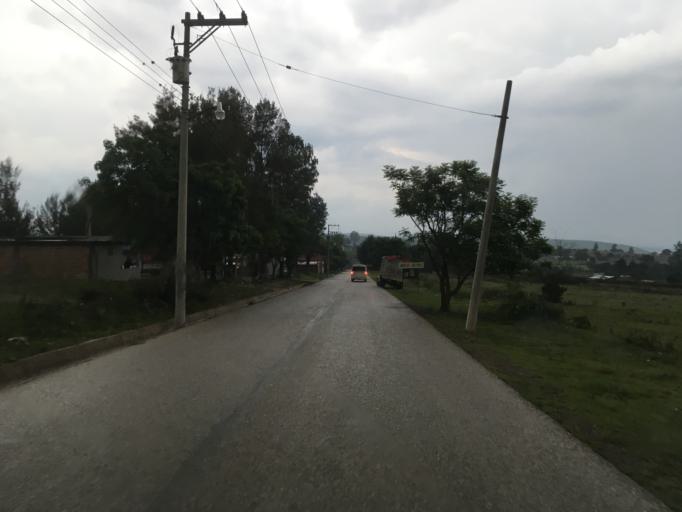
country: MX
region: Oaxaca
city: Santiago Tilantongo
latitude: 17.2888
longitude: -97.2830
